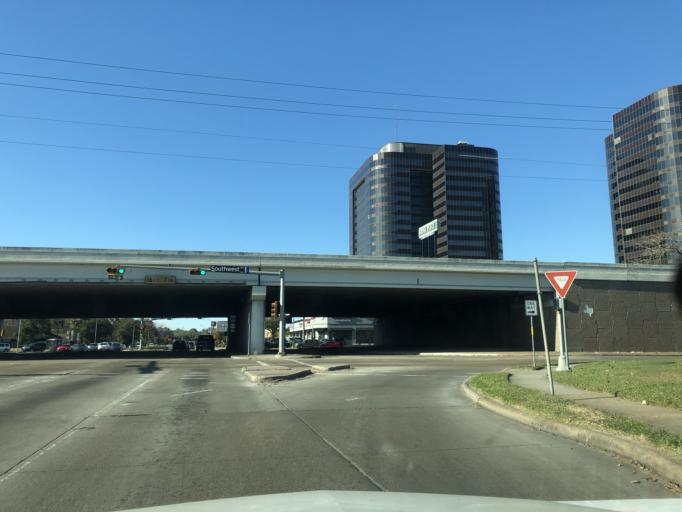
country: US
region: Texas
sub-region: Harris County
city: Bellaire
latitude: 29.6999
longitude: -95.5171
